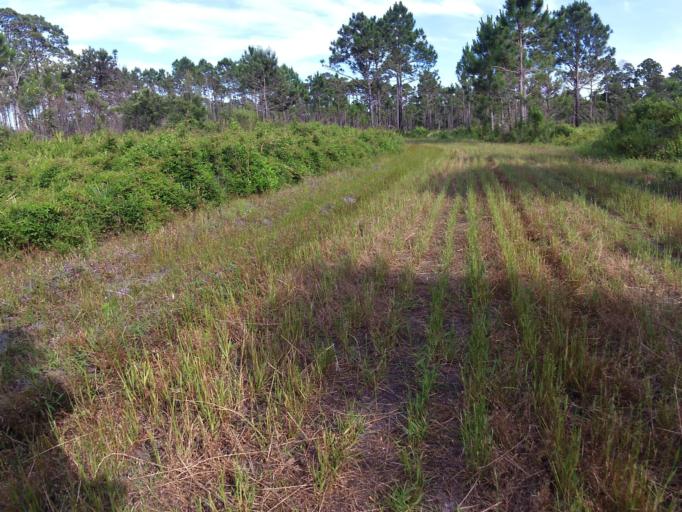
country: US
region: Florida
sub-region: Saint Johns County
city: Villano Beach
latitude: 30.0268
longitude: -81.3434
